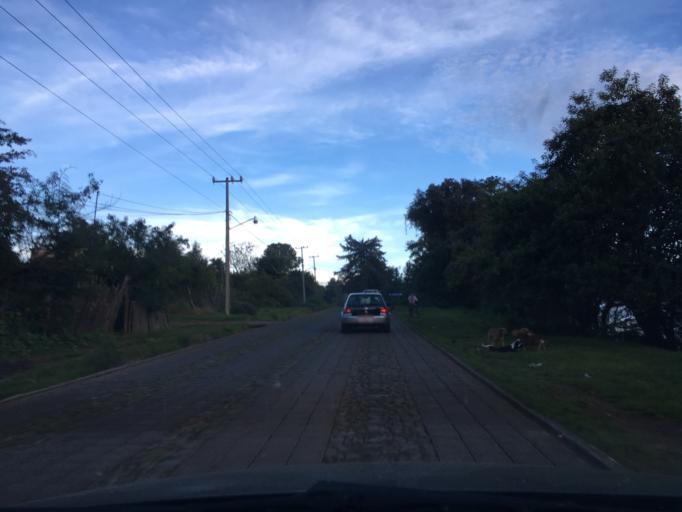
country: MX
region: Michoacan
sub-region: Salvador Escalante
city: Santa Clara del Cobre
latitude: 19.4035
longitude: -101.6557
